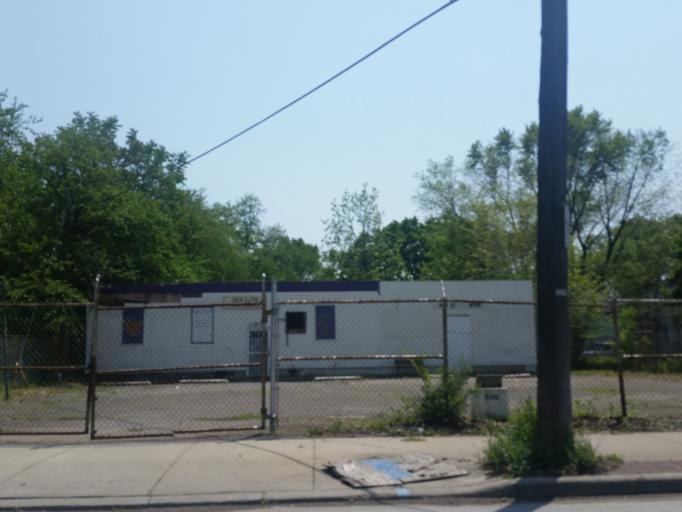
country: US
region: Ohio
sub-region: Cuyahoga County
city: Bratenahl
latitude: 41.4934
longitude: -81.6291
